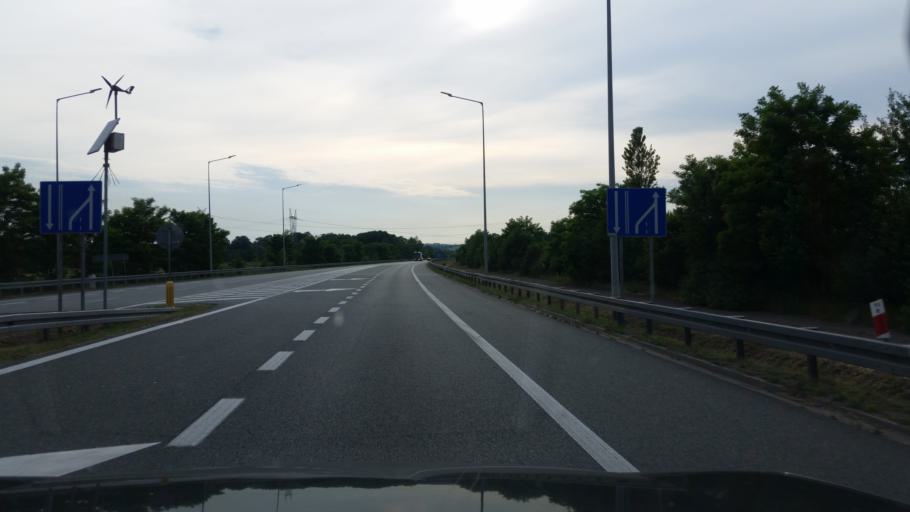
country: PL
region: Silesian Voivodeship
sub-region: Powiat bedzinski
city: Siewierz
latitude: 50.4204
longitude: 19.1981
